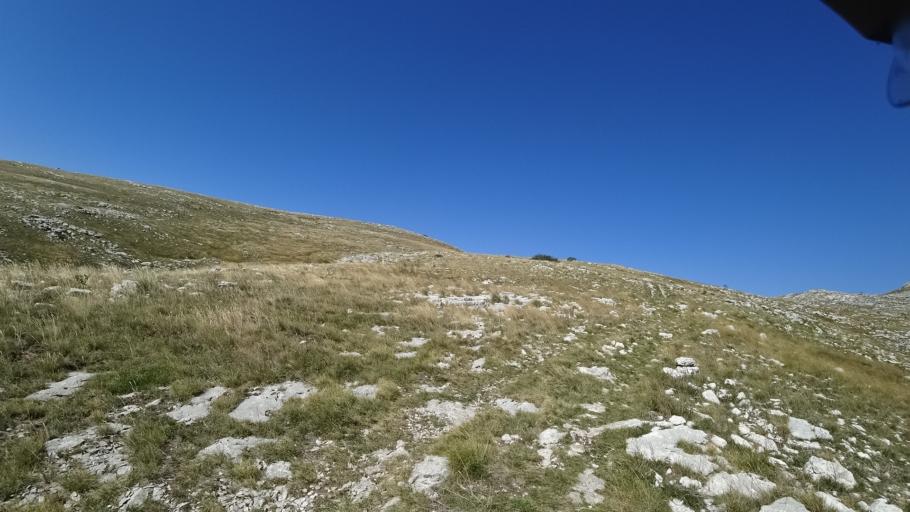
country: HR
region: Splitsko-Dalmatinska
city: Hrvace
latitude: 43.9224
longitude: 16.6055
